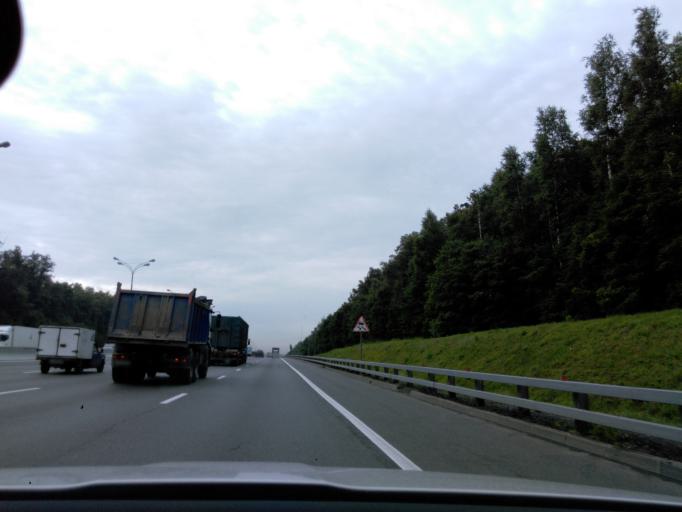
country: RU
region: Moscow
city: Gol'yanovo
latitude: 55.8390
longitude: 37.8101
